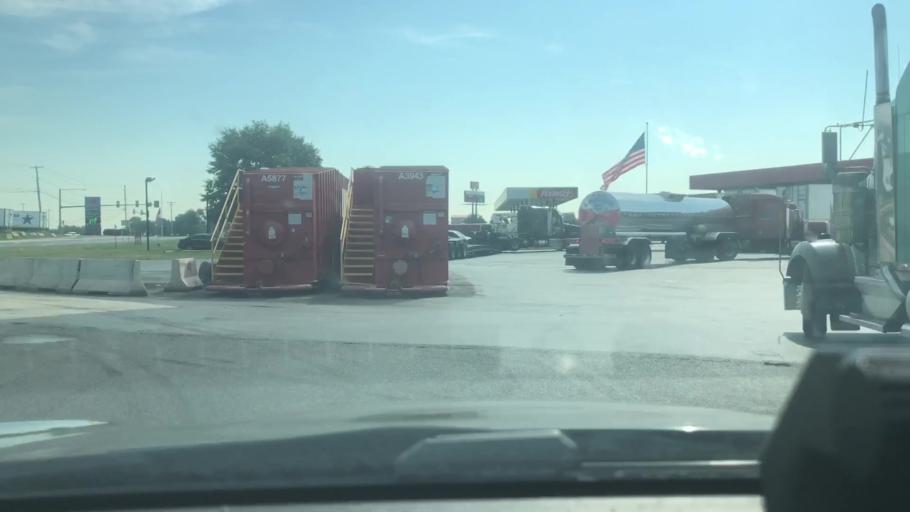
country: US
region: Pennsylvania
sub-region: Dauphin County
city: Skyline View
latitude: 40.3532
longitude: -76.7283
